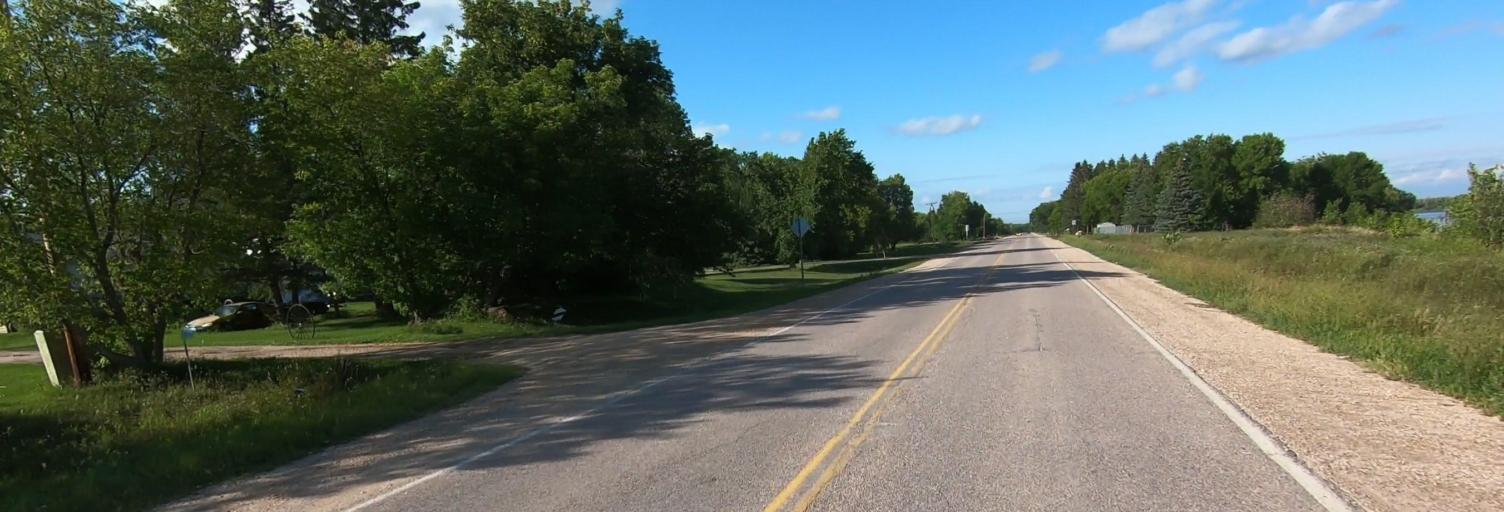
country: CA
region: Manitoba
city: Selkirk
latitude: 50.1927
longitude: -96.8442
